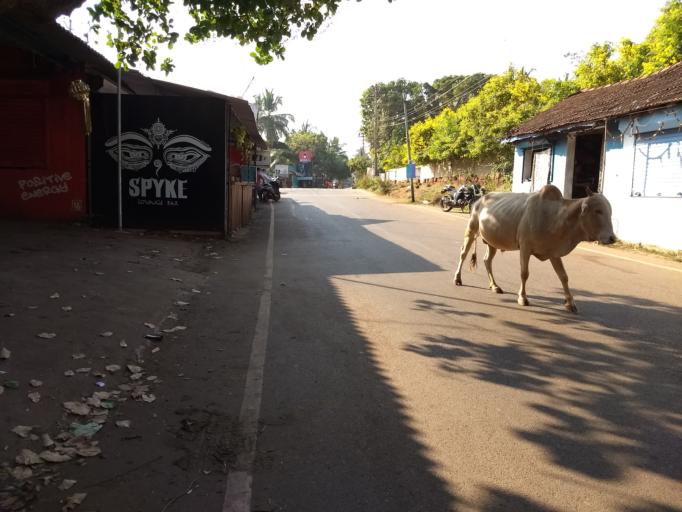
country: IN
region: Goa
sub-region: North Goa
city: Vagator
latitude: 15.5963
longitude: 73.7445
